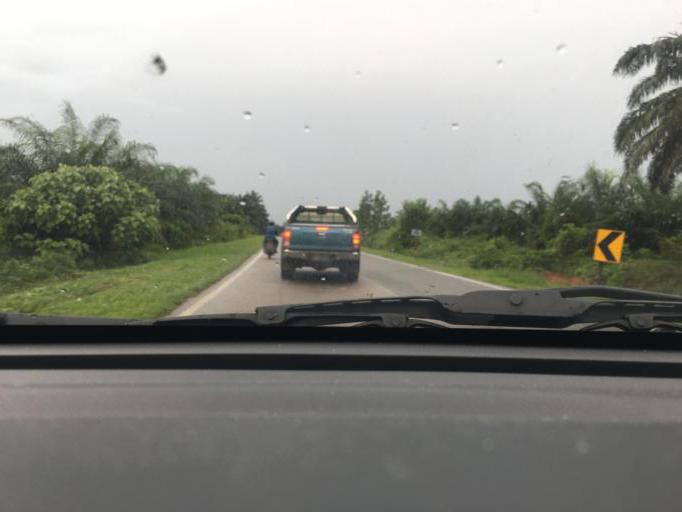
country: MY
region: Kedah
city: Bedong
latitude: 5.6600
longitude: 100.6308
